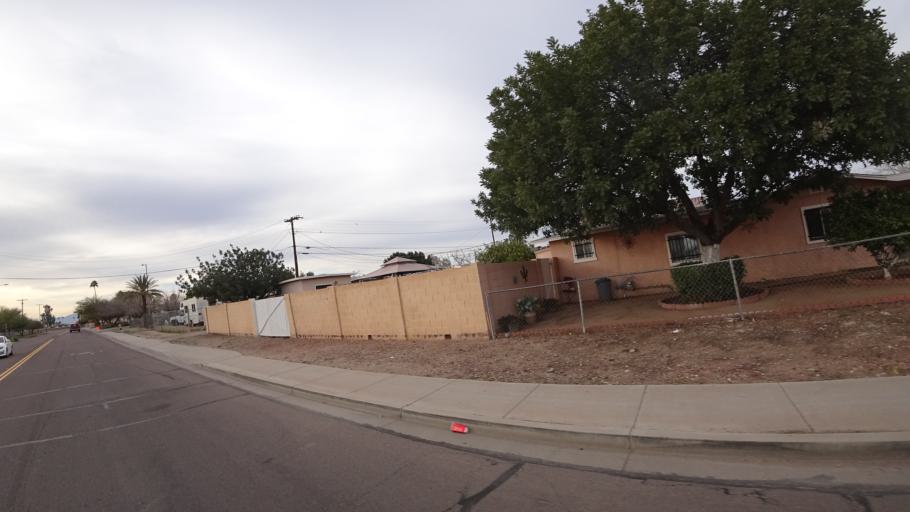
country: US
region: Arizona
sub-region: Maricopa County
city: Surprise
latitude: 33.6235
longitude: -112.3271
